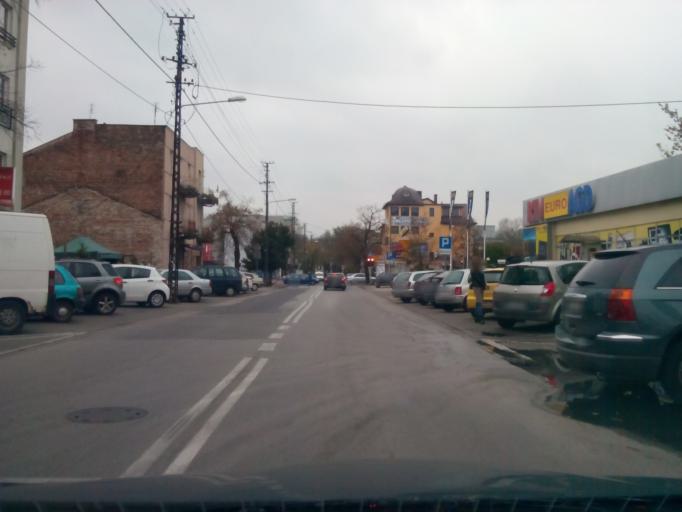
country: PL
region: Masovian Voivodeship
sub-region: Powiat pruszkowski
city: Pruszkow
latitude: 52.1661
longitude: 20.8046
